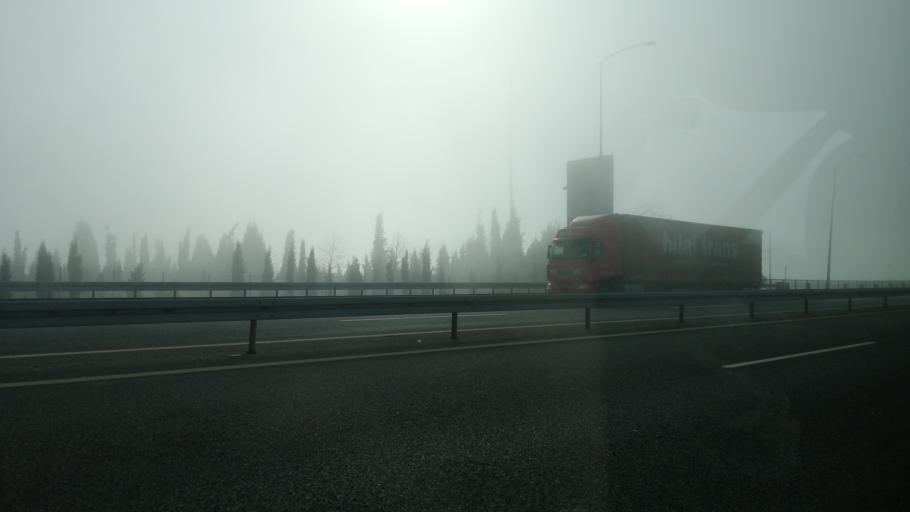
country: TR
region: Kocaeli
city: Tavsanli
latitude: 40.7707
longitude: 29.5182
